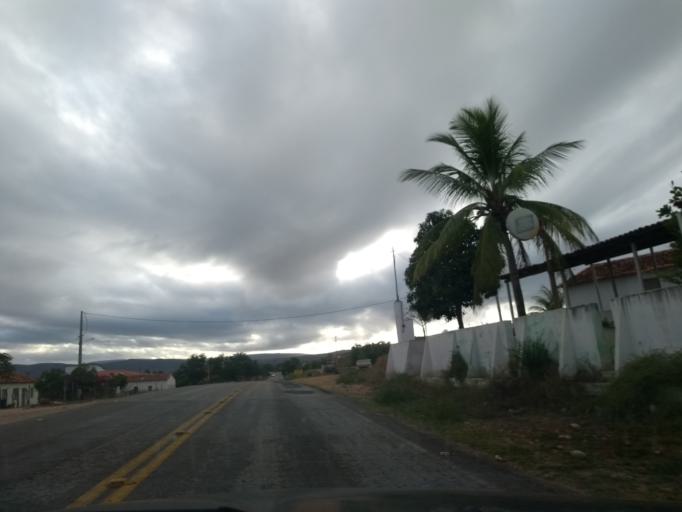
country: BR
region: Bahia
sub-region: Ituacu
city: Ituacu
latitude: -13.7643
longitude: -41.0373
